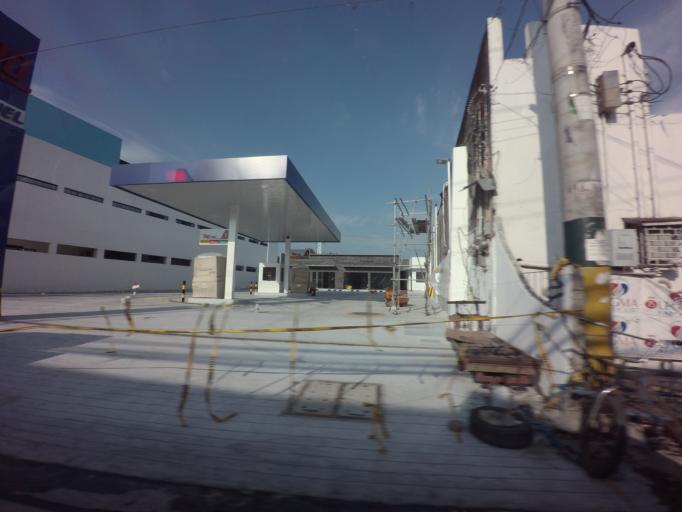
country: PH
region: Calabarzon
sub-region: Province of Rizal
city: Taguig
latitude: 14.4841
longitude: 121.0608
